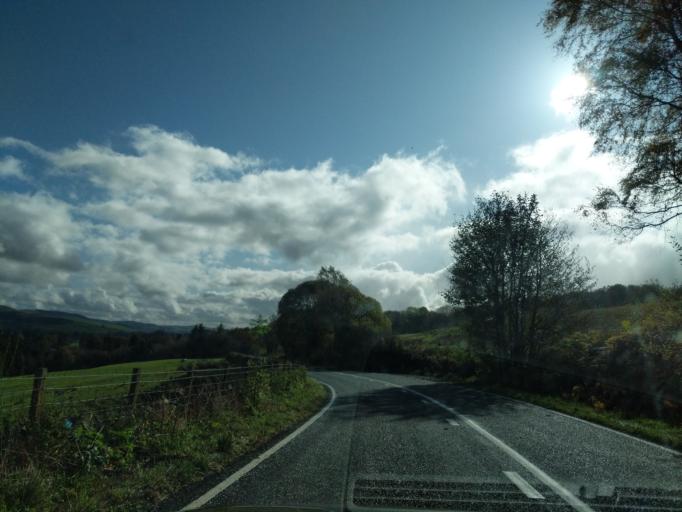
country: GB
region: Scotland
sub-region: Dumfries and Galloway
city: Moffat
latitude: 55.3447
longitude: -3.4603
